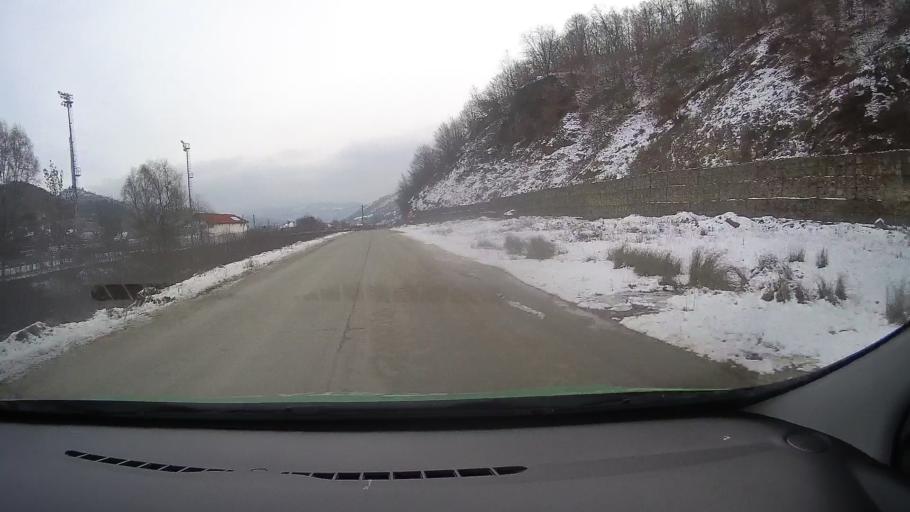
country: RO
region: Alba
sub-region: Oras Zlatna
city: Zlatna
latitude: 46.1149
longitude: 23.2102
